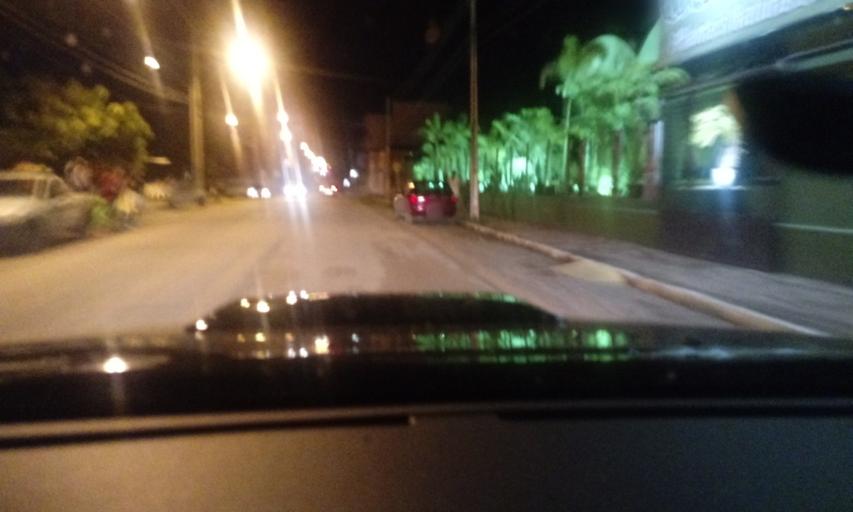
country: BR
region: Bahia
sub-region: Guanambi
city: Guanambi
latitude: -14.2160
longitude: -42.7730
